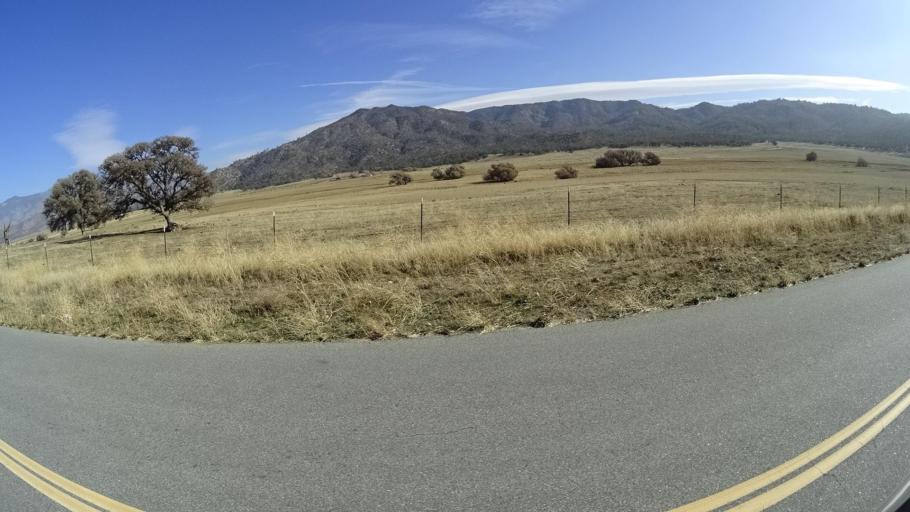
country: US
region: California
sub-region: Kern County
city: Bodfish
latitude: 35.3933
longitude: -118.5508
